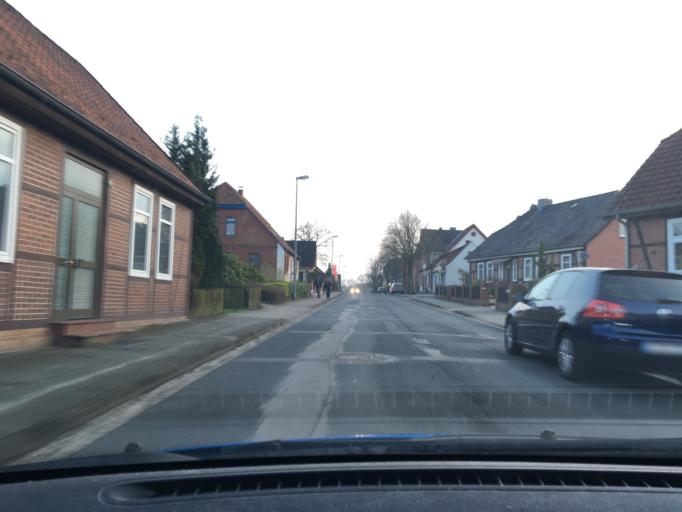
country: DE
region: Lower Saxony
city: Bad Fallingbostel
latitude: 52.9012
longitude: 9.7697
